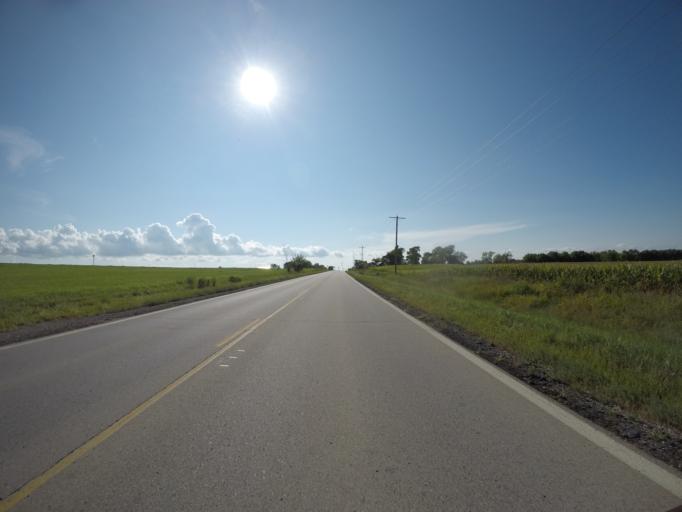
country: US
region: Kansas
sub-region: Leavenworth County
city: Tonganoxie
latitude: 39.1094
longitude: -95.1130
